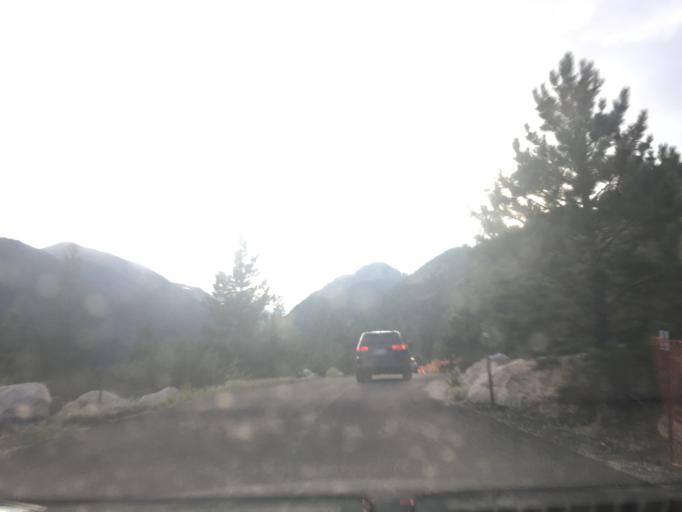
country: US
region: Colorado
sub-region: Larimer County
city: Estes Park
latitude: 40.4099
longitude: -105.6344
